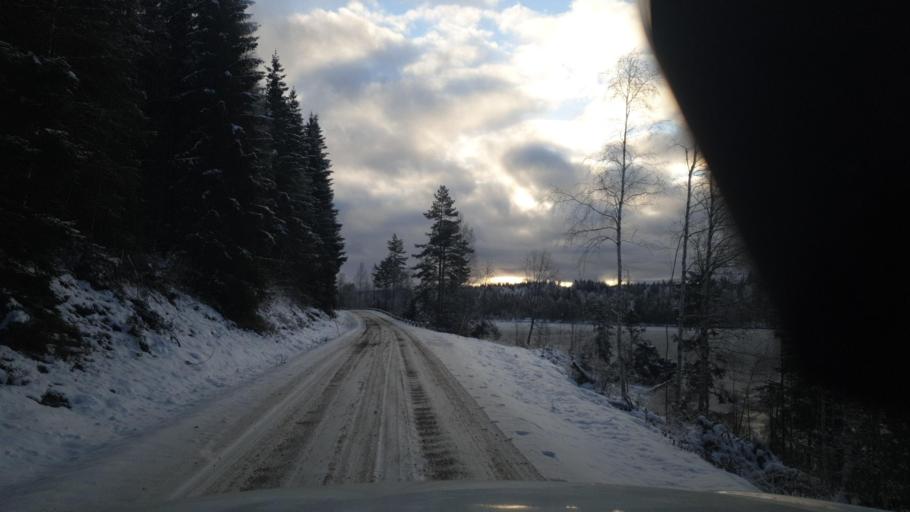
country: SE
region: Vaermland
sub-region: Eda Kommun
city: Charlottenberg
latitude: 60.1089
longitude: 12.6053
